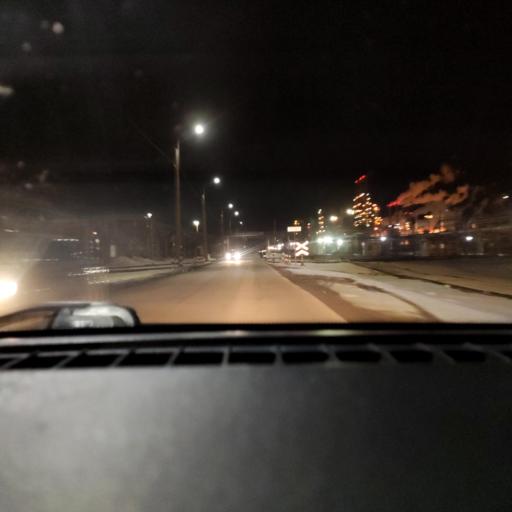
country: RU
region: Perm
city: Gamovo
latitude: 57.9116
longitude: 56.1495
